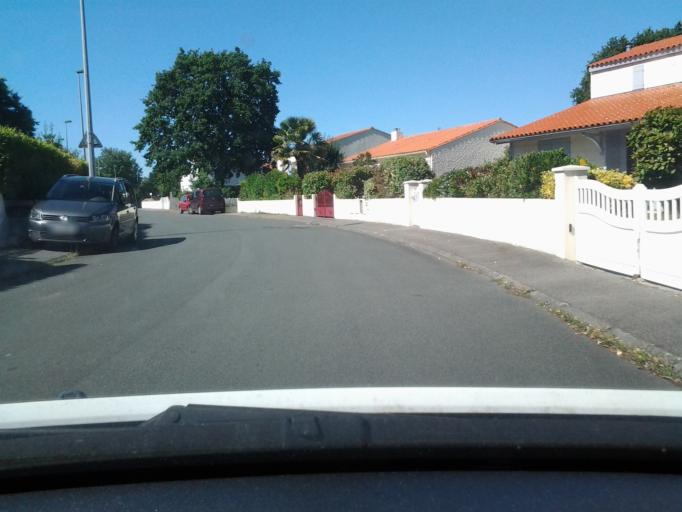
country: FR
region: Pays de la Loire
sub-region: Departement de la Vendee
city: La Roche-sur-Yon
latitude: 46.6626
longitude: -1.4166
